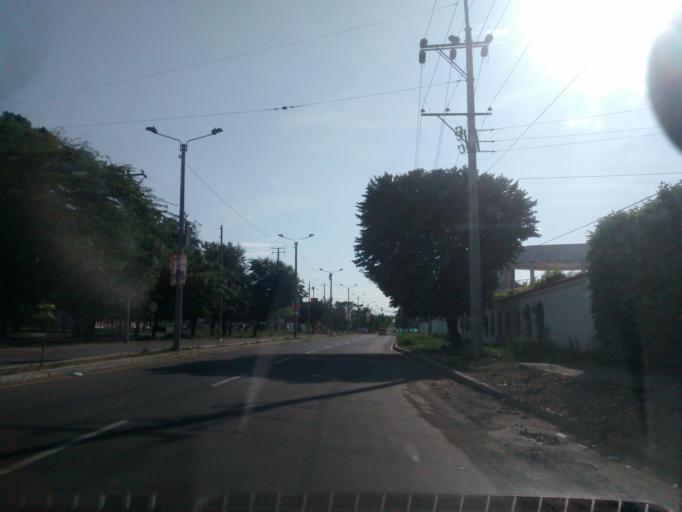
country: CO
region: Cundinamarca
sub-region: Girardot
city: Girardot City
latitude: 4.3066
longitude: -74.8121
